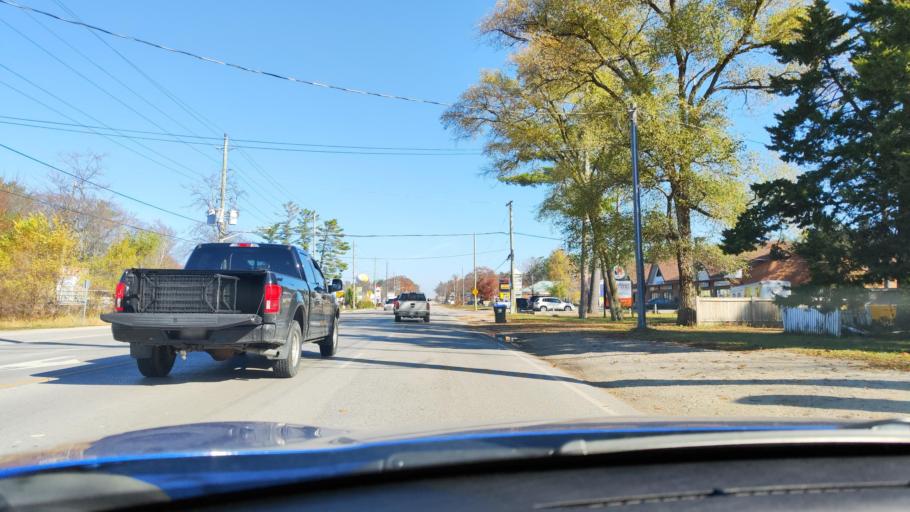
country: CA
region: Ontario
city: Wasaga Beach
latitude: 44.5250
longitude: -80.0002
